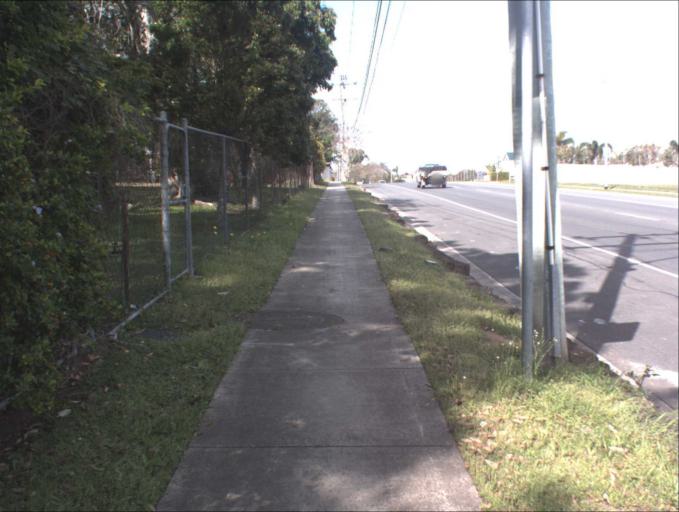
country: AU
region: Queensland
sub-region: Logan
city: Waterford West
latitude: -27.6914
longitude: 153.1203
